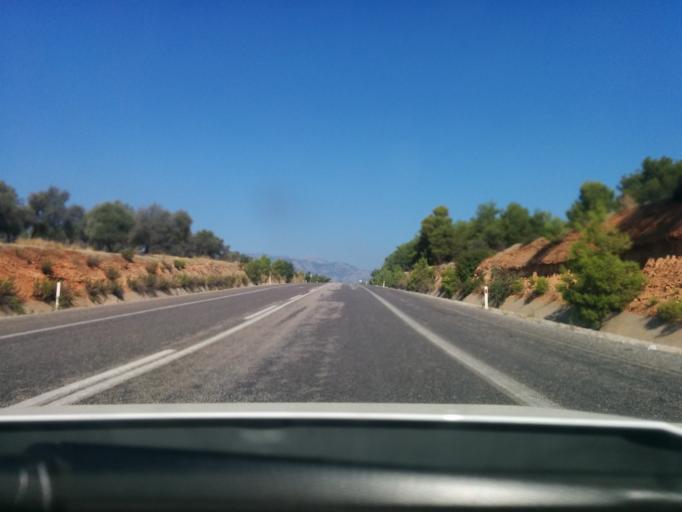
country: TR
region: Mugla
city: Esen
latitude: 36.3665
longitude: 29.3283
